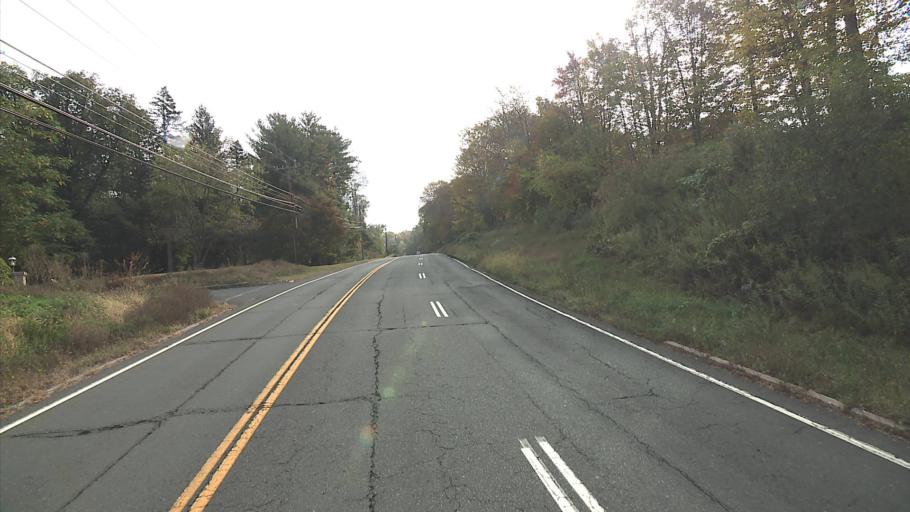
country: US
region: Connecticut
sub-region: Fairfield County
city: Newtown
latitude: 41.4205
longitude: -73.3495
